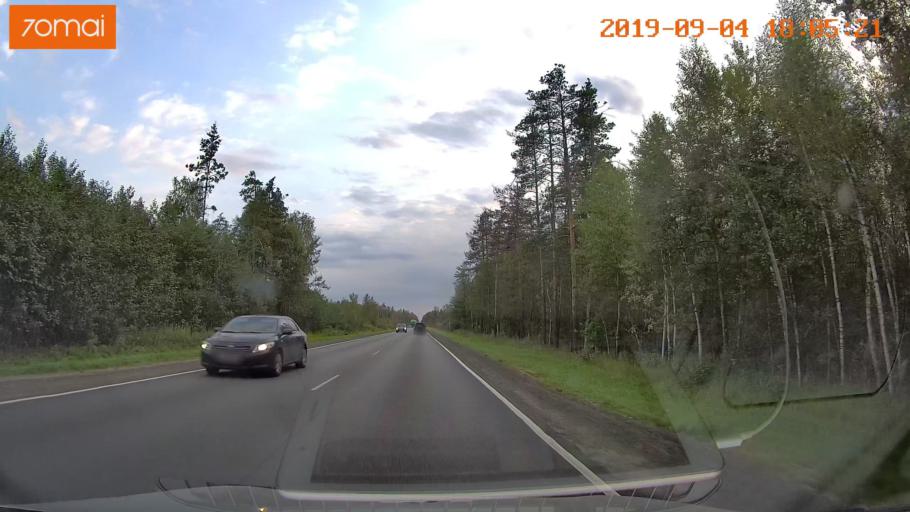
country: RU
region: Moskovskaya
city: Il'inskiy Pogost
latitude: 55.4423
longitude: 38.8277
